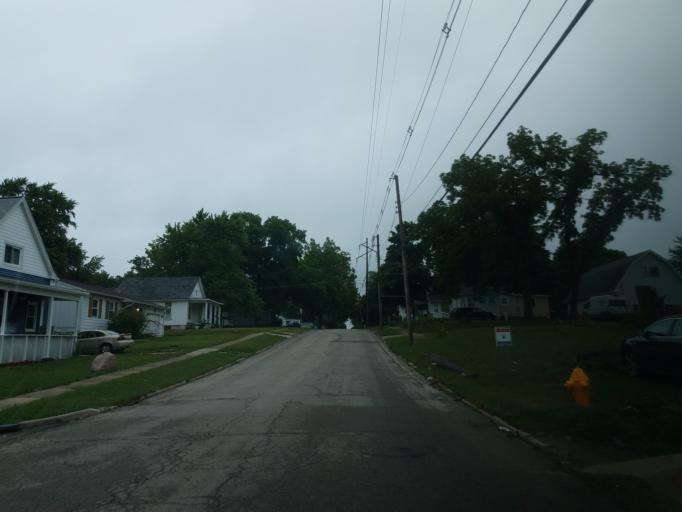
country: US
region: Illinois
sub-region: McLean County
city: Bloomington
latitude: 40.4694
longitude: -88.9819
